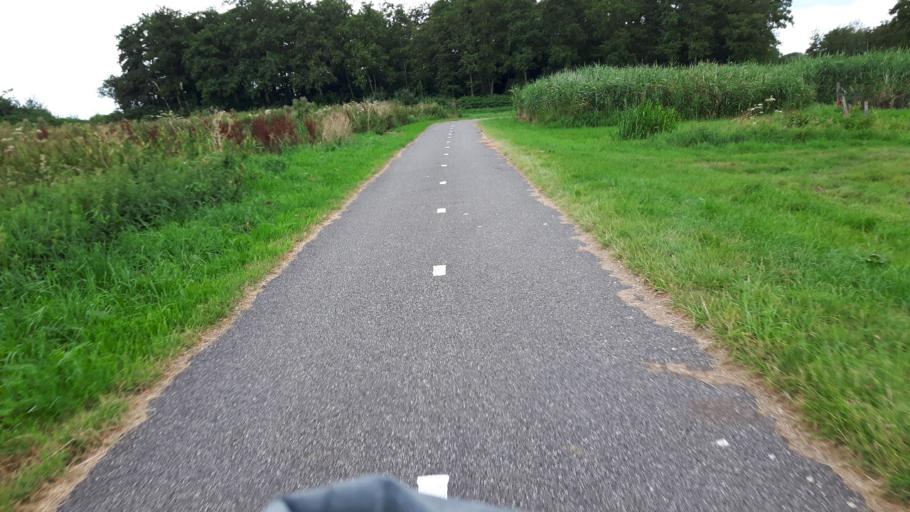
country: NL
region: South Holland
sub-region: Molenwaard
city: Nieuw-Lekkerland
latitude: 51.9285
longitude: 4.7431
